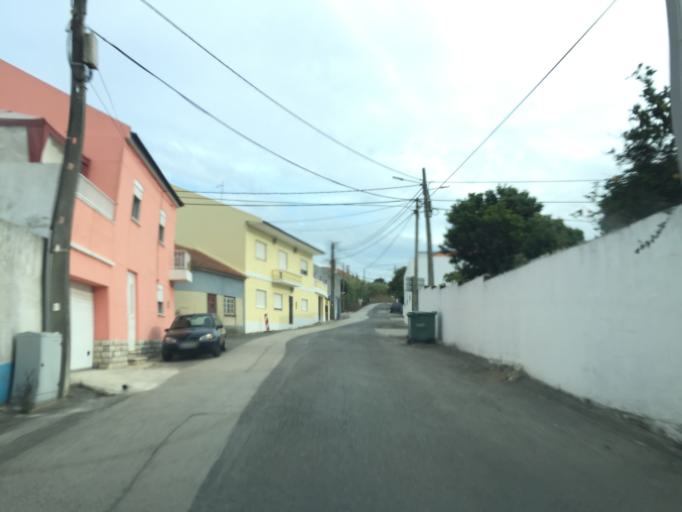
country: PT
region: Leiria
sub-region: Peniche
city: Atouguia da Baleia
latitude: 39.3386
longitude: -9.2988
